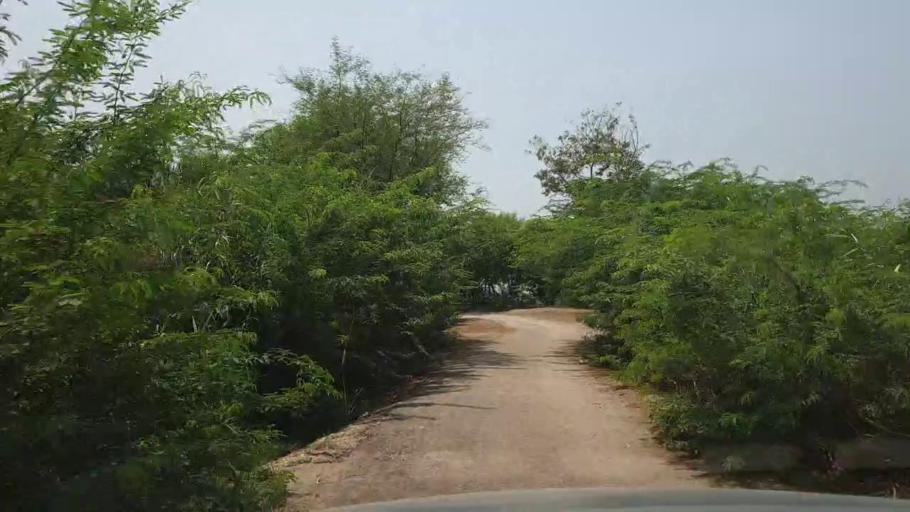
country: PK
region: Sindh
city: Garhi Yasin
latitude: 27.8765
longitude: 68.5008
